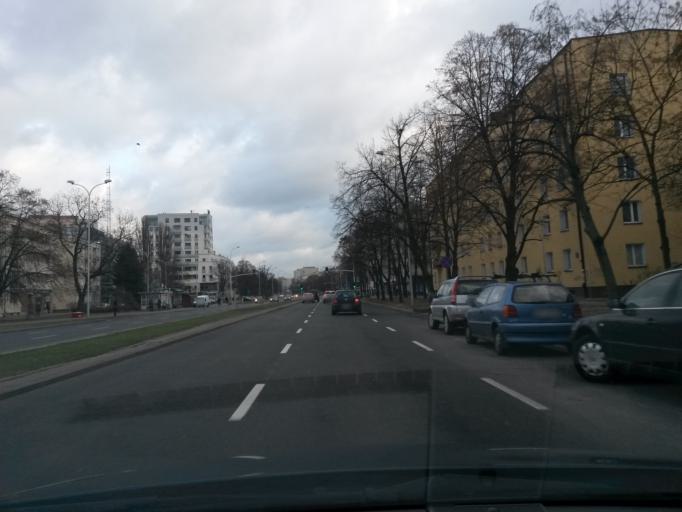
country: PL
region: Masovian Voivodeship
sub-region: Warszawa
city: Mokotow
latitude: 52.2068
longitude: 21.0348
